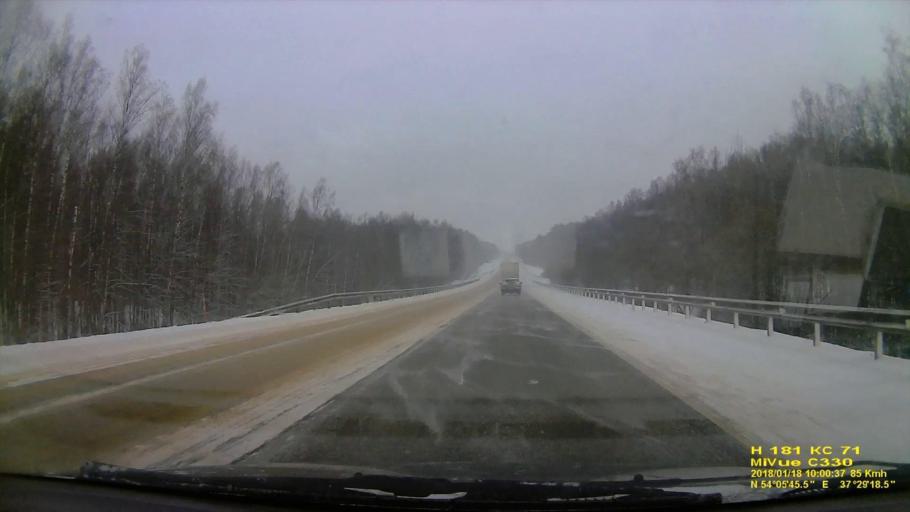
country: RU
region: Tula
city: Pervomayskiy
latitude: 54.0957
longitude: 37.4885
